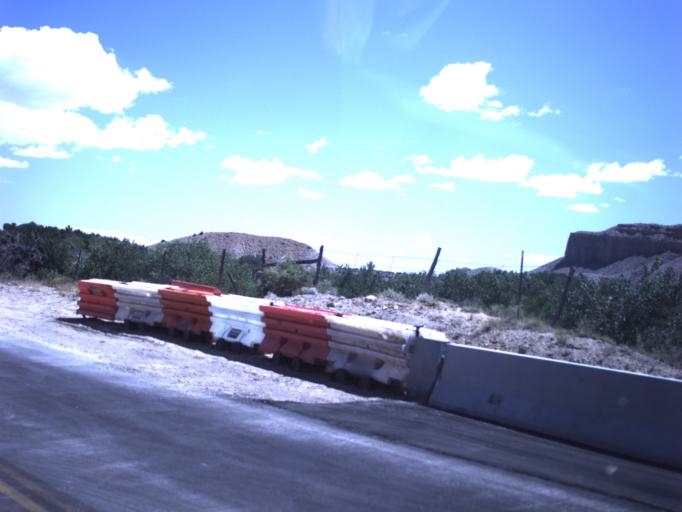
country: US
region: Utah
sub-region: Emery County
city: Orangeville
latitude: 39.2605
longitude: -111.1183
